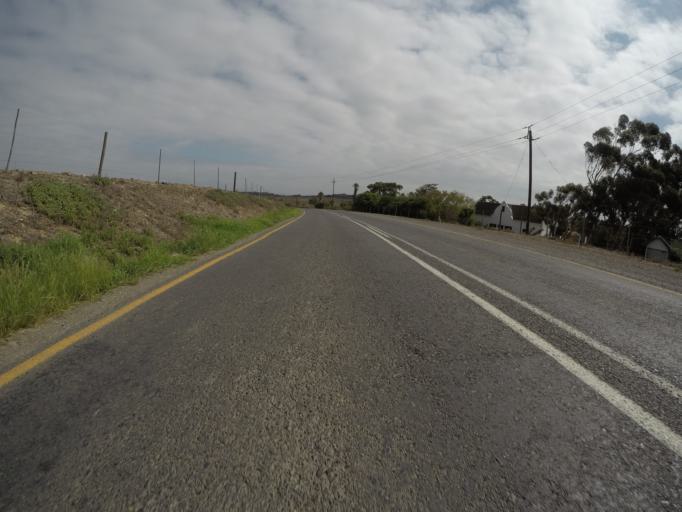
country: ZA
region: Western Cape
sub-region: City of Cape Town
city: Sunset Beach
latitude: -33.7818
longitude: 18.5574
